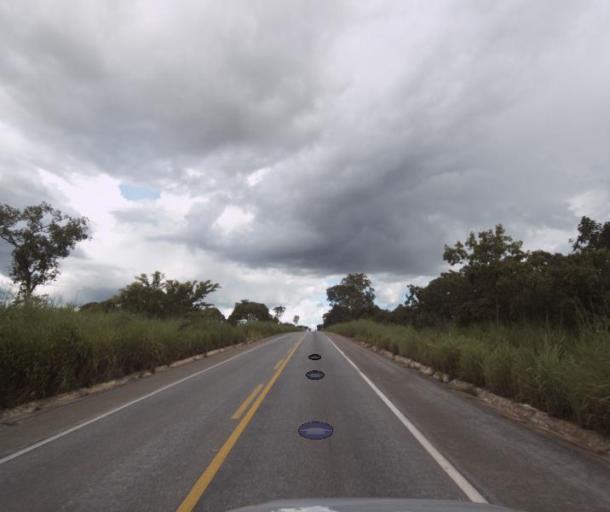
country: BR
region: Goias
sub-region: Porangatu
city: Porangatu
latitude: -13.3040
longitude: -49.1202
